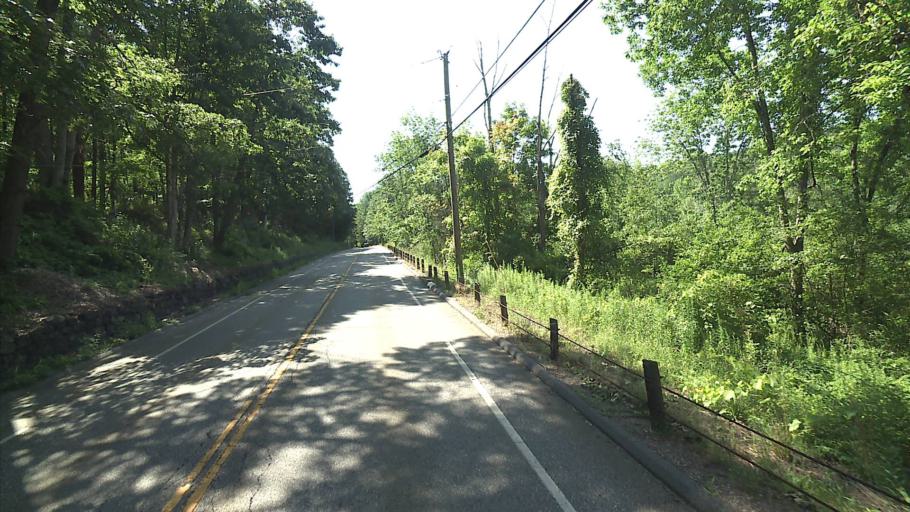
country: US
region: Connecticut
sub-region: Litchfield County
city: New Preston
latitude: 41.7925
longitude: -73.3662
